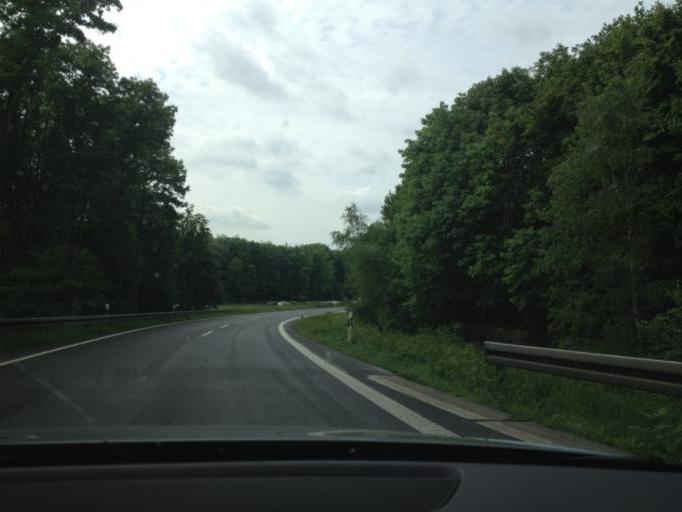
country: DE
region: North Rhine-Westphalia
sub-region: Regierungsbezirk Dusseldorf
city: Oberhausen
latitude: 51.5372
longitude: 6.8308
